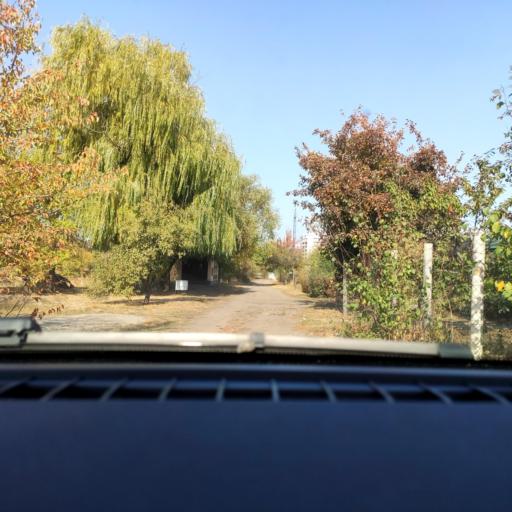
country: RU
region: Voronezj
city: Maslovka
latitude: 51.6071
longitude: 39.2164
